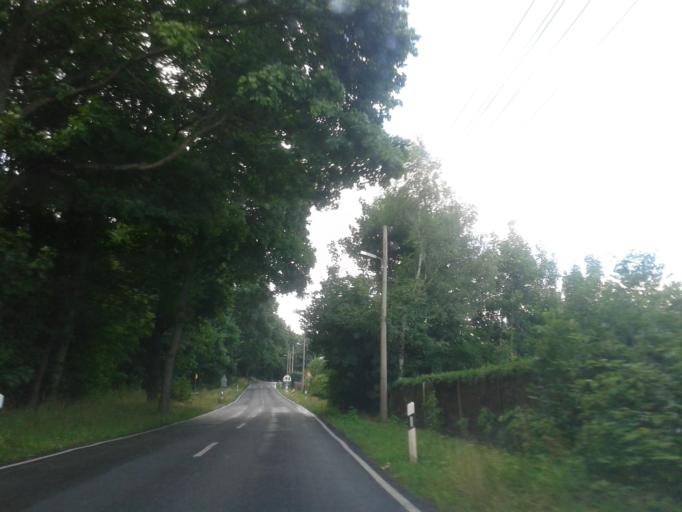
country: DE
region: Saxony
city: Radeberg
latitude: 51.0749
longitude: 13.8876
